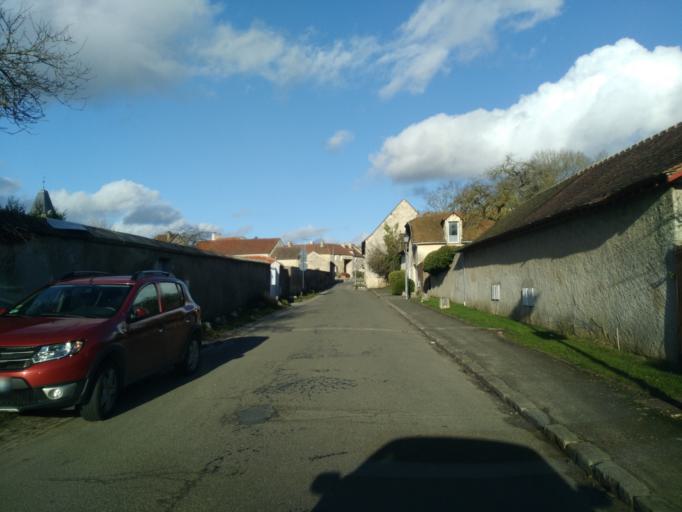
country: FR
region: Ile-de-France
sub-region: Departement des Yvelines
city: Saint-Nom-la-Breteche
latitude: 48.8547
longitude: 2.0186
